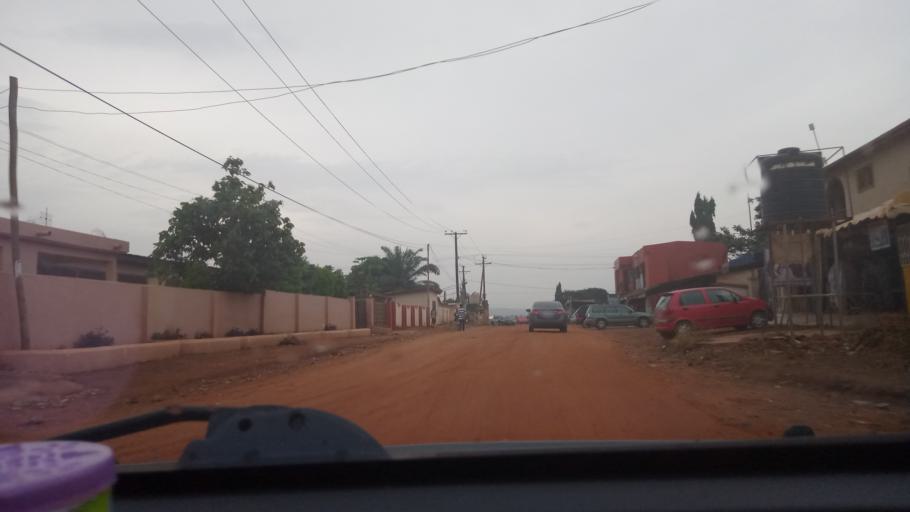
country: GH
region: Greater Accra
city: Medina Estates
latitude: 5.7053
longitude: -0.1670
